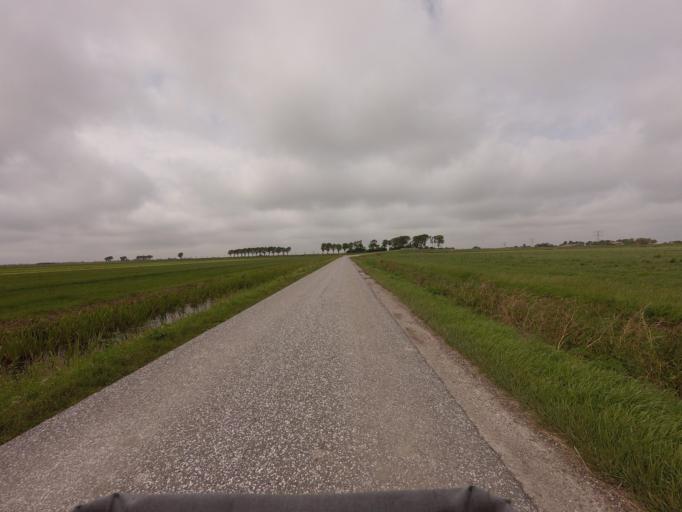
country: NL
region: North Holland
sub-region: Gemeente Schagen
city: Schagen
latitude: 52.7976
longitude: 4.8257
